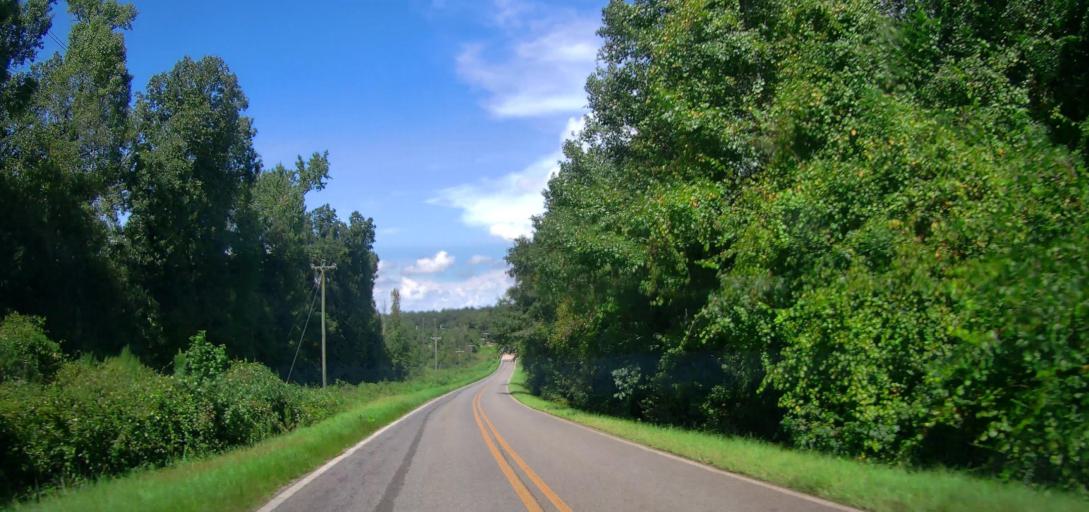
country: US
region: Georgia
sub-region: Macon County
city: Marshallville
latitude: 32.4754
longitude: -83.8668
